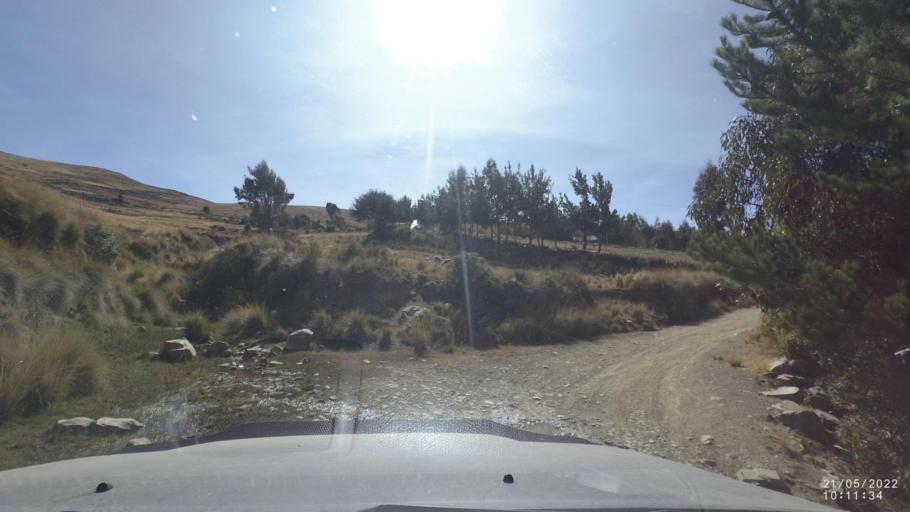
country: BO
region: Cochabamba
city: Colomi
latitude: -17.3312
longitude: -65.9808
